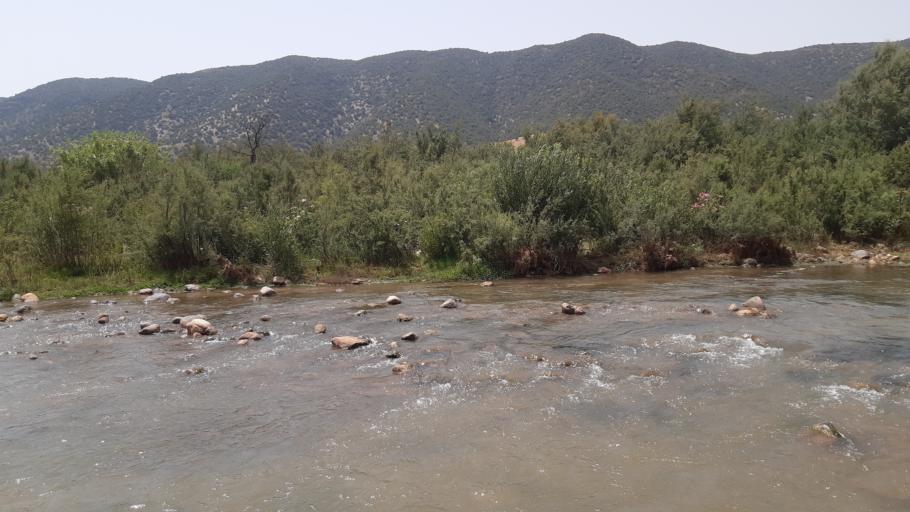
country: MA
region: Meknes-Tafilalet
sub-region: Khenifra
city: Khenifra
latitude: 33.0759
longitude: -5.5366
